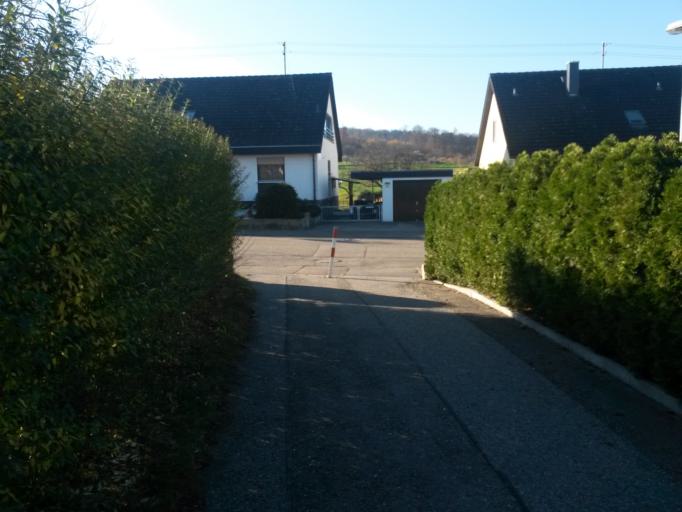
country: DE
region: Baden-Wuerttemberg
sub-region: Karlsruhe Region
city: Neuenburg
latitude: 48.8688
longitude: 8.5880
